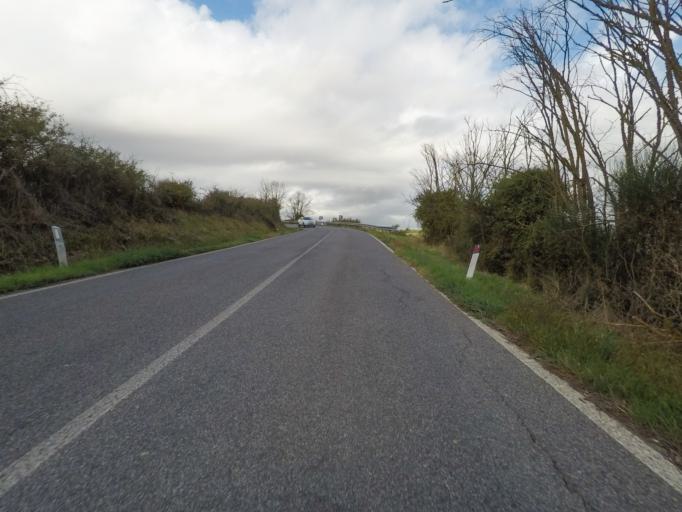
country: IT
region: Tuscany
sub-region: Provincia di Siena
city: Belverde
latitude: 43.3633
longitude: 11.3277
